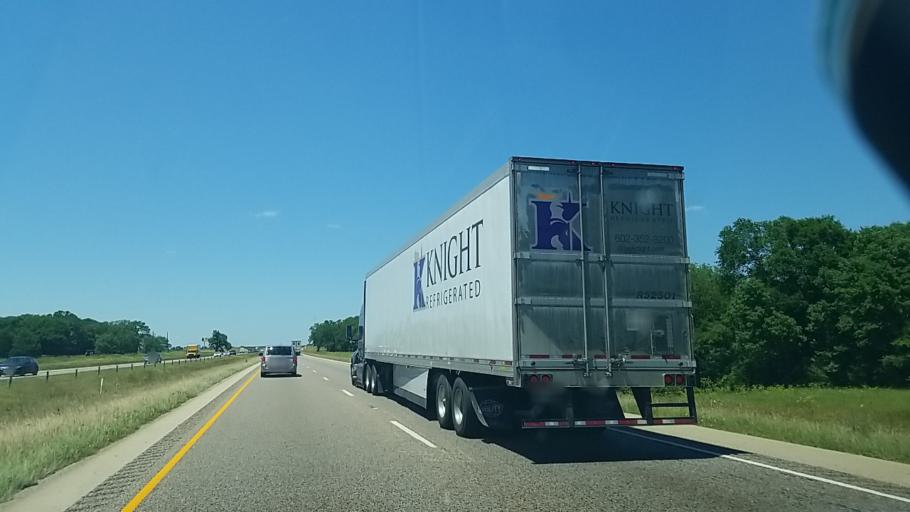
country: US
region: Texas
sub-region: Madison County
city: Madisonville
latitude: 31.0848
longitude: -95.9583
